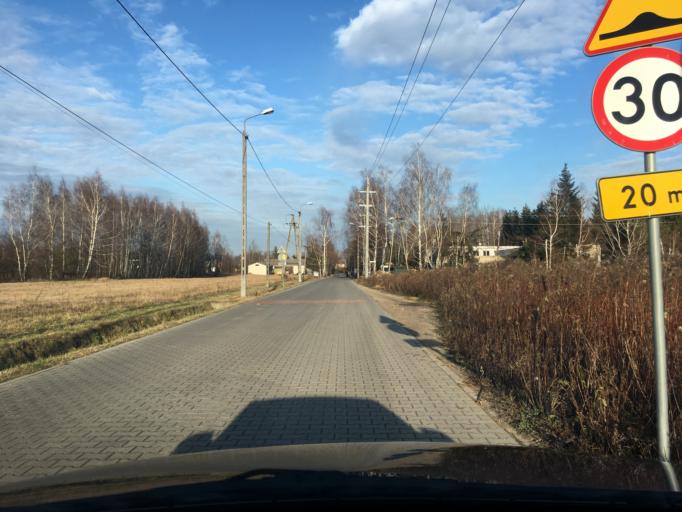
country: PL
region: Masovian Voivodeship
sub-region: Powiat piaseczynski
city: Lesznowola
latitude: 52.0330
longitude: 20.9394
